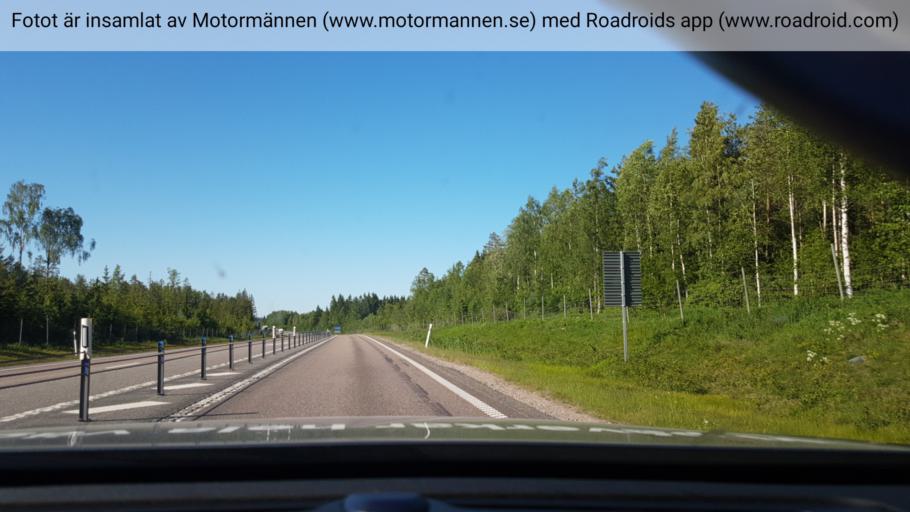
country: SE
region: Vaesternorrland
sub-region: Sundsvalls Kommun
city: Njurundabommen
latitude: 62.2063
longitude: 17.3748
